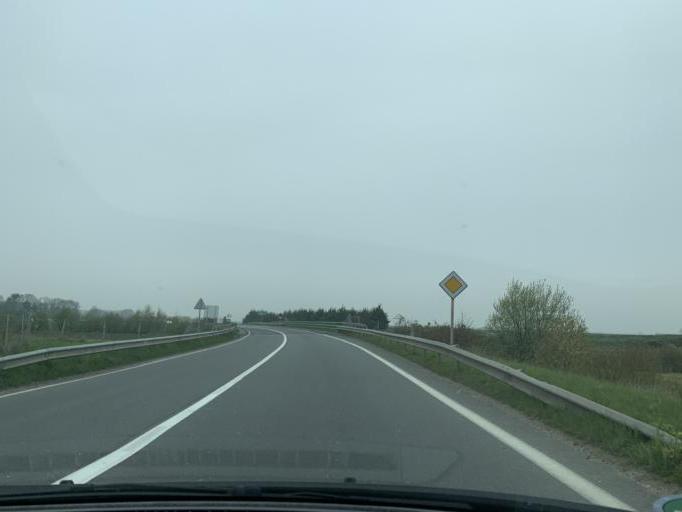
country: FR
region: Picardie
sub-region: Departement de la Somme
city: Abbeville
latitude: 50.1323
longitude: 1.8282
